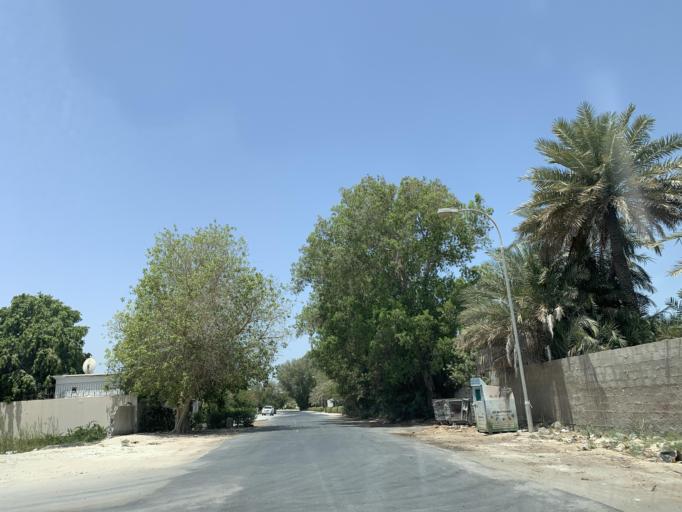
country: BH
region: Manama
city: Jidd Hafs
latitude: 26.2265
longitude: 50.4705
